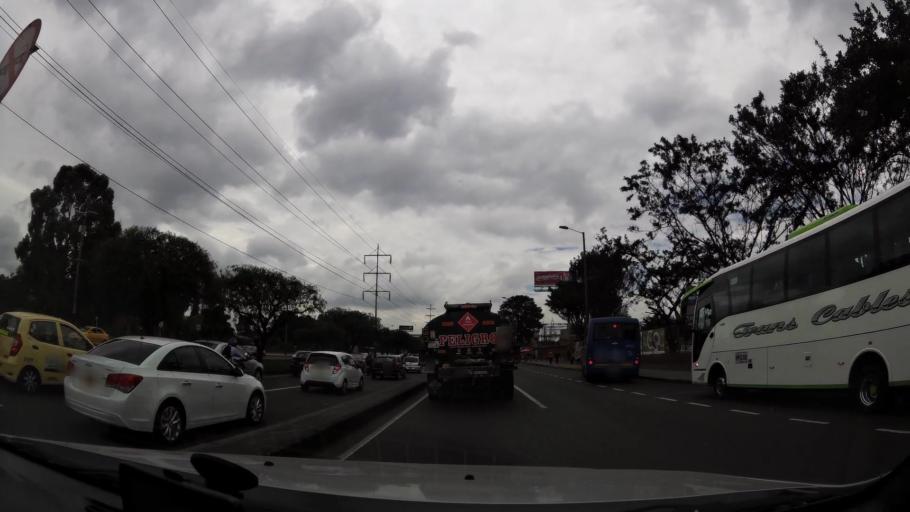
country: CO
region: Bogota D.C.
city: Bogota
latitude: 4.6595
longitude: -74.0990
